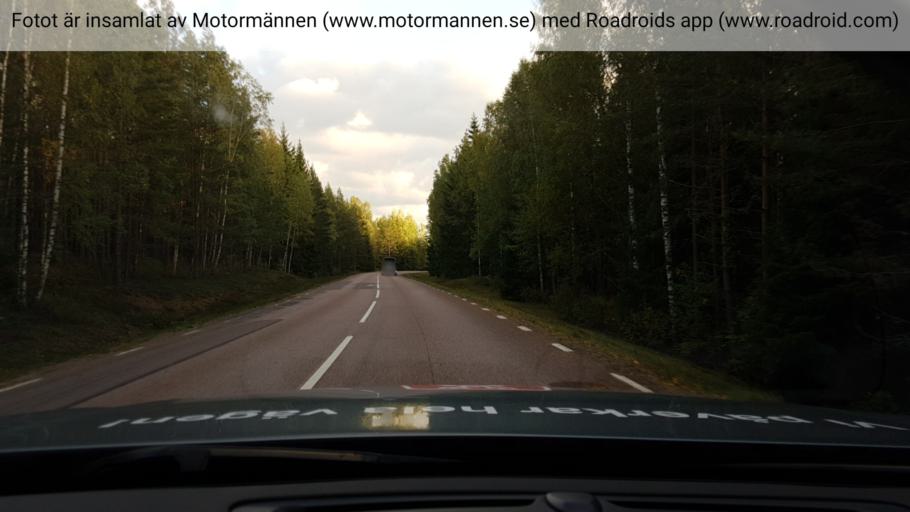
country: SE
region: Vaermland
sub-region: Karlstads Kommun
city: Molkom
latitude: 59.5023
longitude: 13.7960
